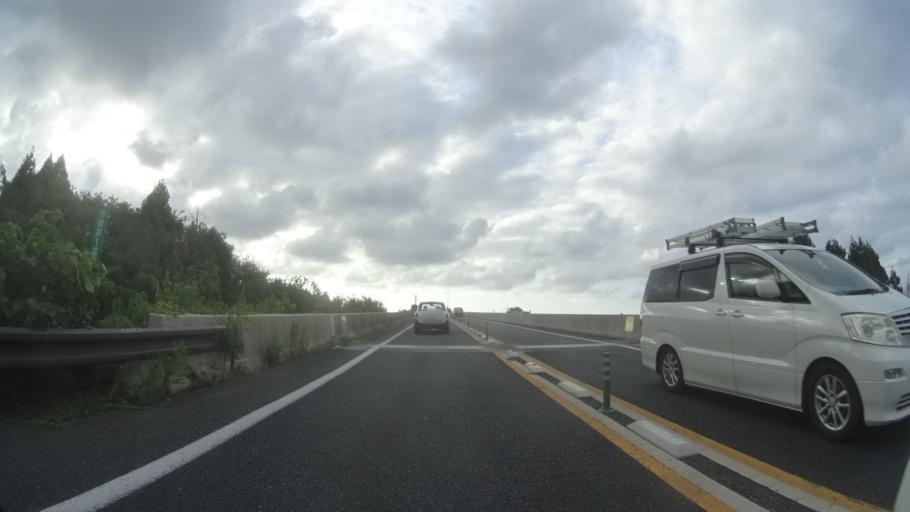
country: JP
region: Tottori
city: Kurayoshi
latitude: 35.5054
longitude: 133.6501
